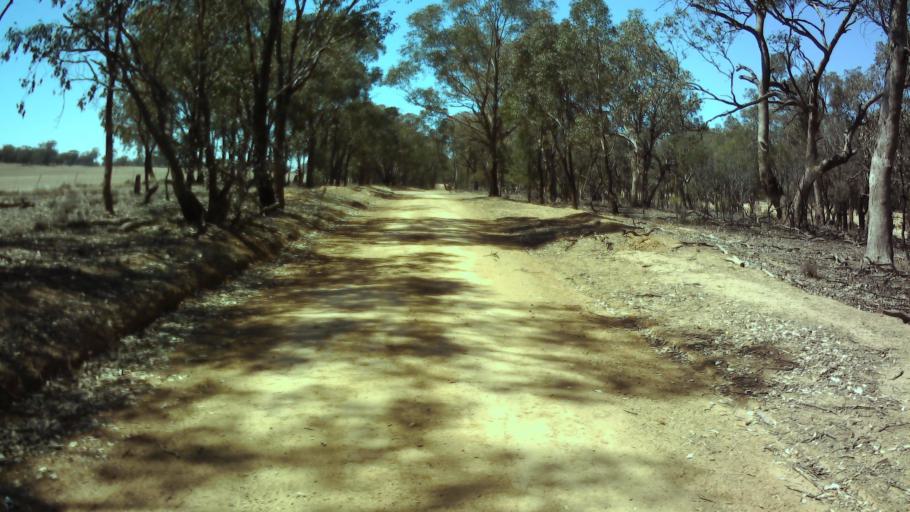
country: AU
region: New South Wales
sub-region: Weddin
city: Grenfell
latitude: -33.9578
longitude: 148.0854
